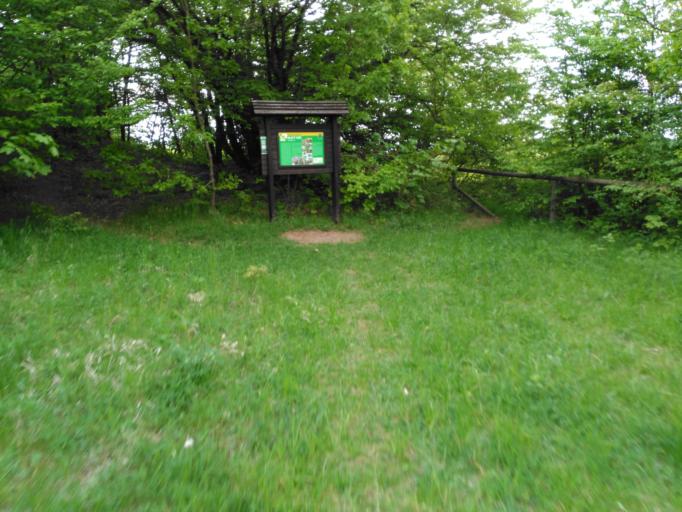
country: CZ
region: Central Bohemia
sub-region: Okres Beroun
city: Beroun
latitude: 49.9132
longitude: 14.0794
